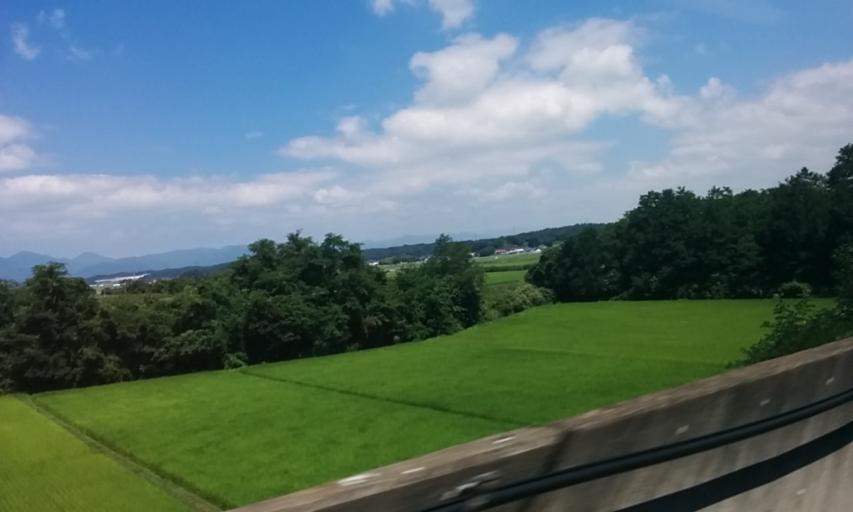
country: JP
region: Fukushima
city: Sukagawa
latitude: 37.2556
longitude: 140.3061
